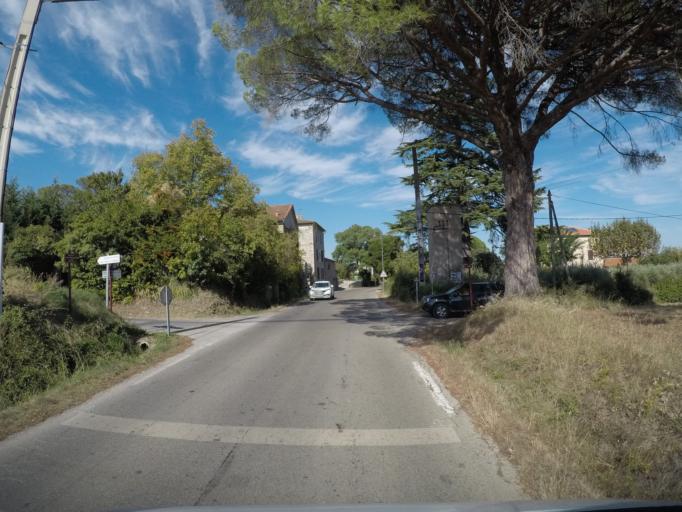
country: FR
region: Languedoc-Roussillon
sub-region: Departement du Gard
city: Boisset-et-Gaujac
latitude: 44.0202
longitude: 3.9950
